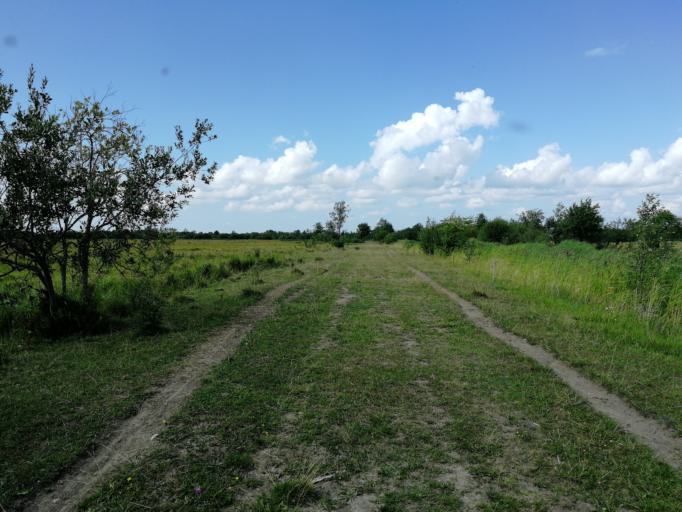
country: EE
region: Laeaene
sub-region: Lihula vald
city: Lihula
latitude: 58.7218
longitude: 23.8085
